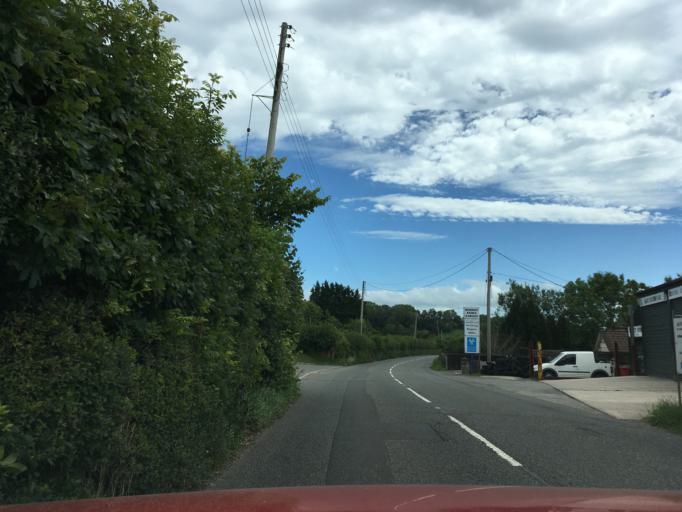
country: GB
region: England
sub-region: Somerset
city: Bradley Cross
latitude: 51.2503
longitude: -2.7418
